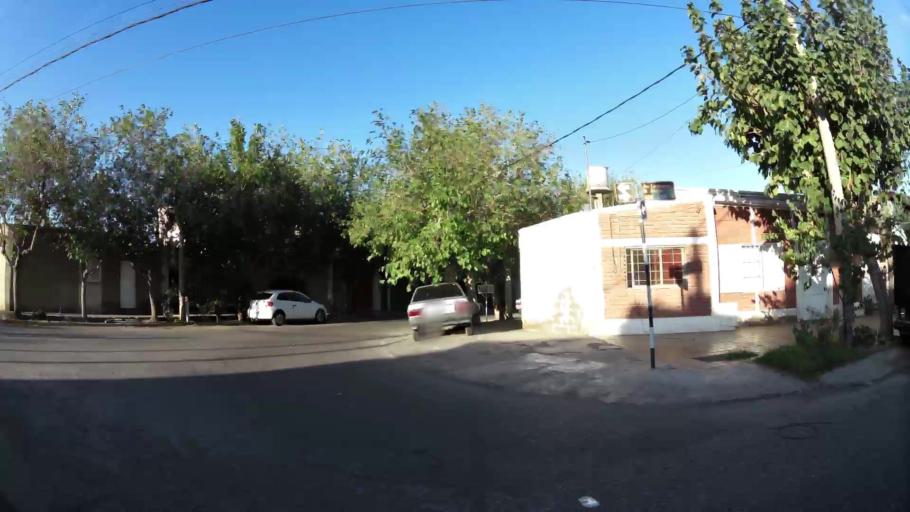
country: AR
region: San Juan
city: San Juan
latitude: -31.5485
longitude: -68.5285
